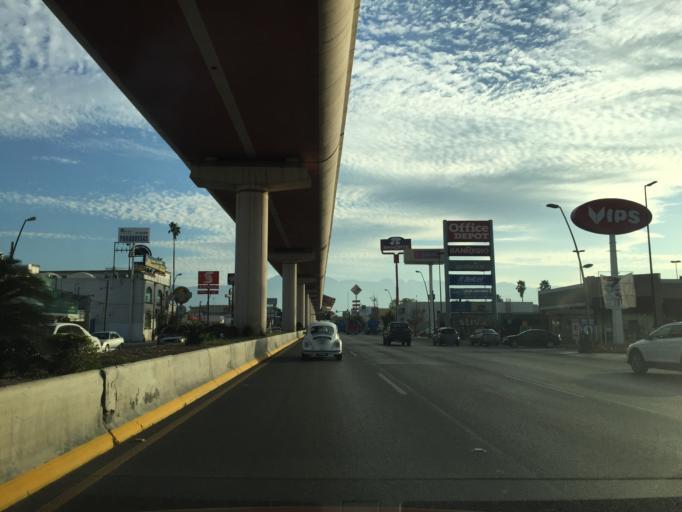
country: MX
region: Nuevo Leon
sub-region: San Nicolas de los Garza
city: San Nicolas de los Garza
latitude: 25.7433
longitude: -100.3014
